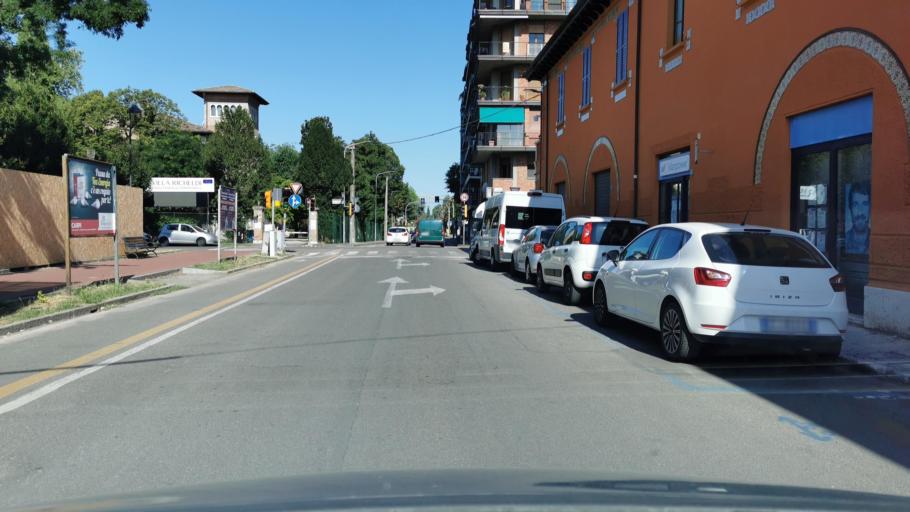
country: IT
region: Emilia-Romagna
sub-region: Provincia di Modena
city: Carpi Centro
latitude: 44.7835
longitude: 10.8811
